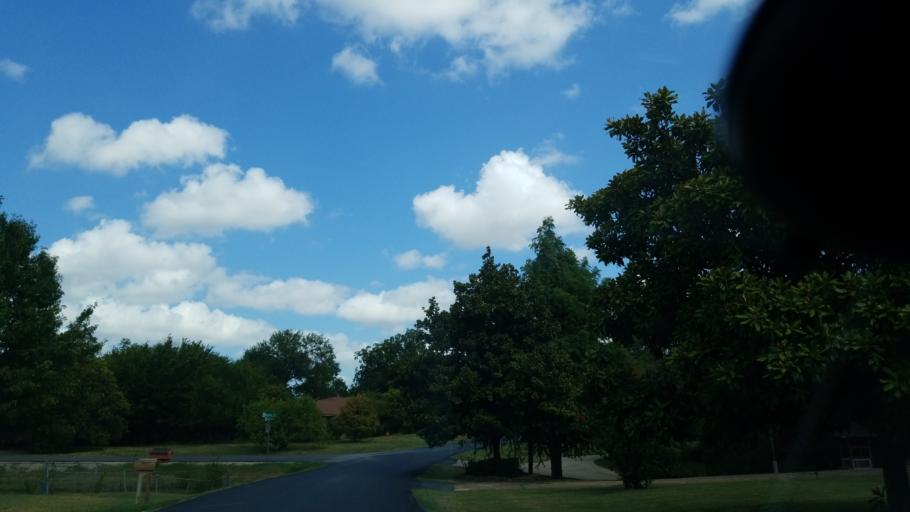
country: US
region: Texas
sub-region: Dallas County
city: Grand Prairie
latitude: 32.7130
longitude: -96.9962
